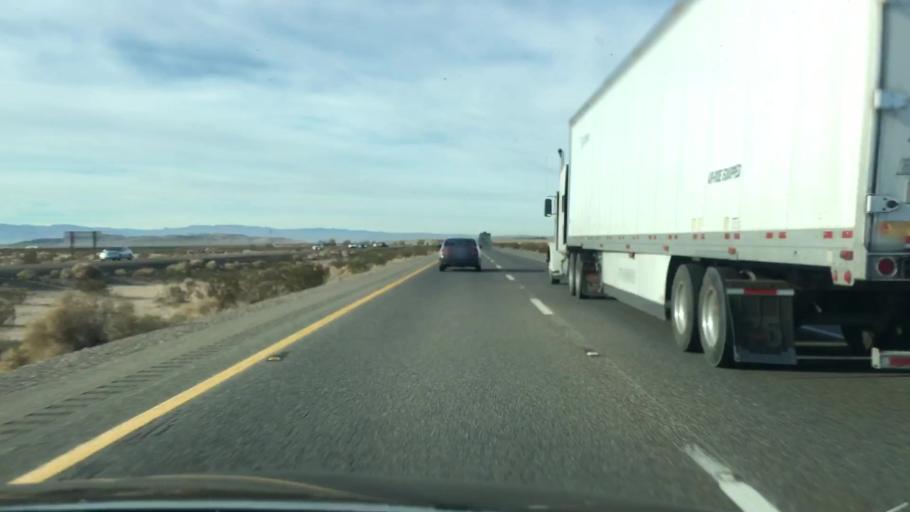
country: US
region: California
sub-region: San Bernardino County
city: Fort Irwin
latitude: 34.9699
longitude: -116.6313
